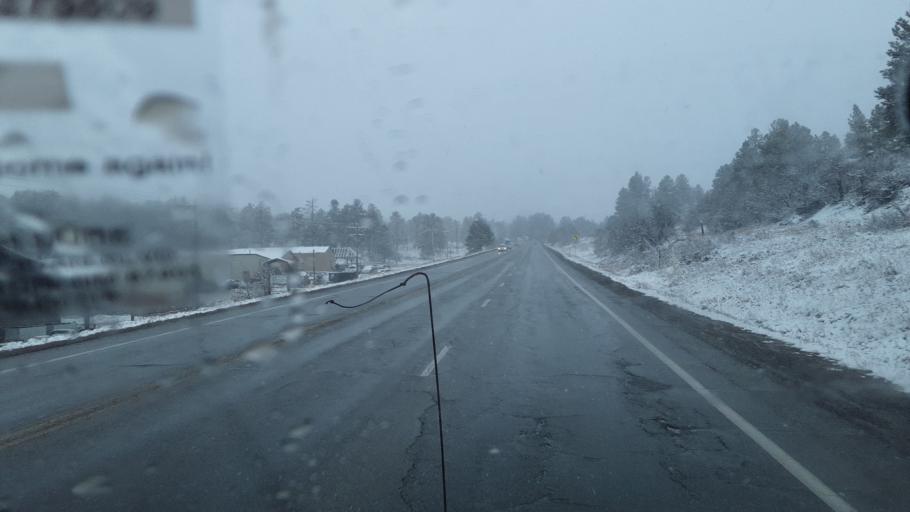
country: US
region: Colorado
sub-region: Archuleta County
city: Pagosa Springs
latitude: 37.2696
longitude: -107.0304
